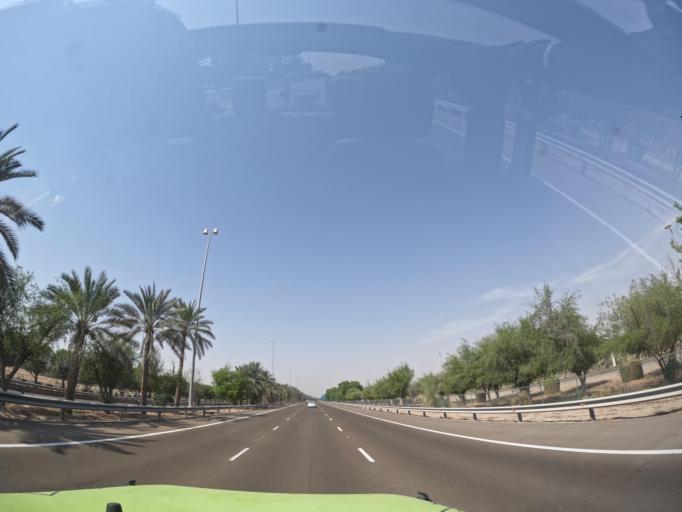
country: AE
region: Abu Dhabi
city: Al Ain
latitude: 24.1786
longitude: 55.3149
